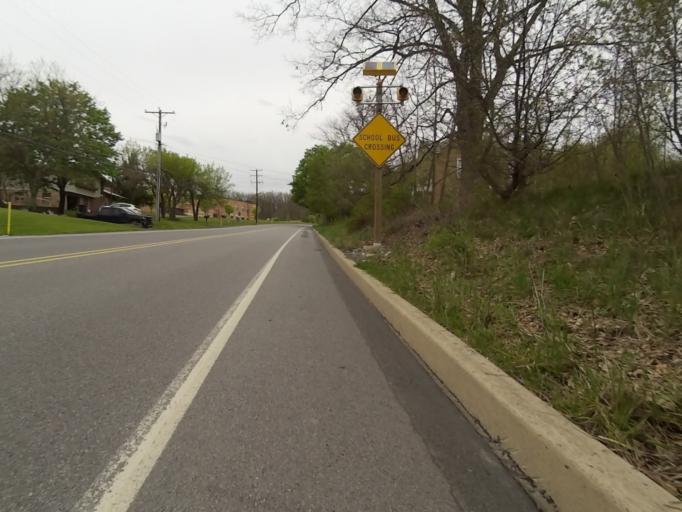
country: US
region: Pennsylvania
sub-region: Clearfield County
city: Troy
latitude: 40.9049
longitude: -78.2000
